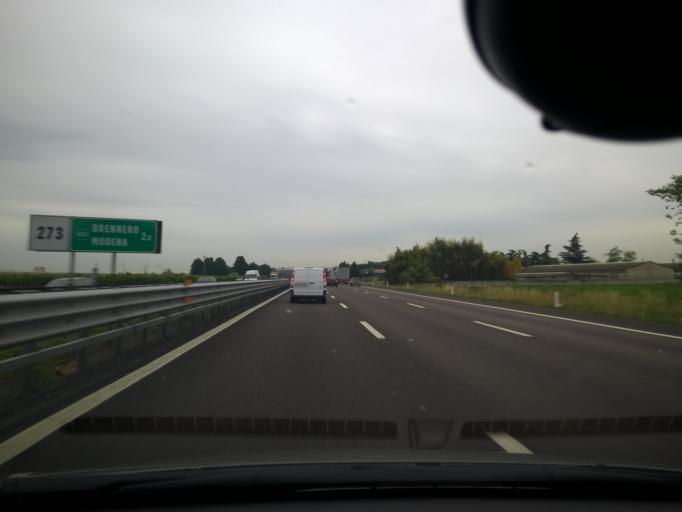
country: IT
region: Veneto
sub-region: Provincia di Verona
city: Caselle
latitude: 45.4138
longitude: 10.8796
